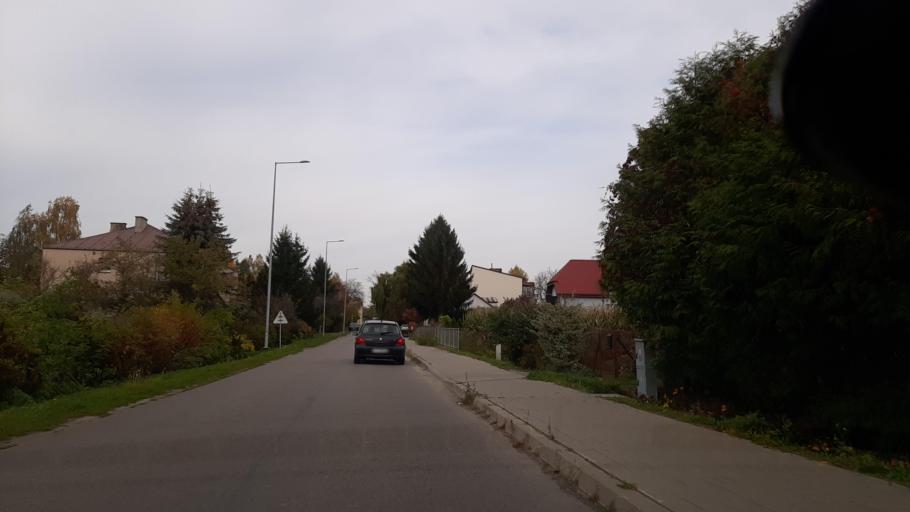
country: PL
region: Lublin Voivodeship
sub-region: Powiat pulawski
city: Naleczow
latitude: 51.3152
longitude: 22.2135
